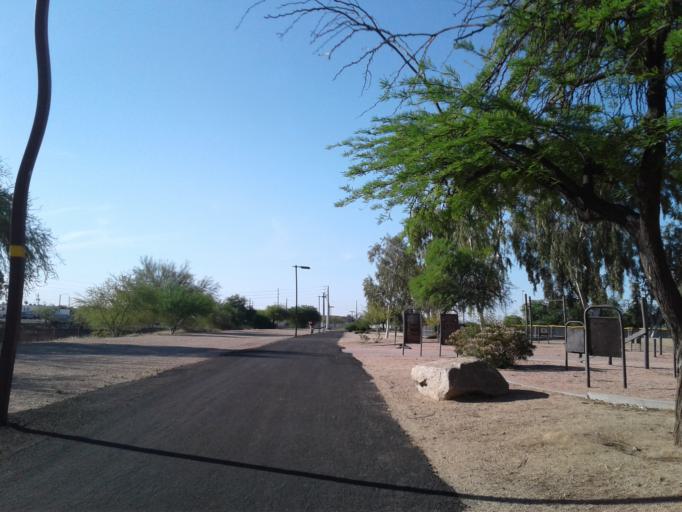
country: US
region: Arizona
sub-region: Maricopa County
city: Glendale
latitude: 33.5764
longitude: -112.1100
